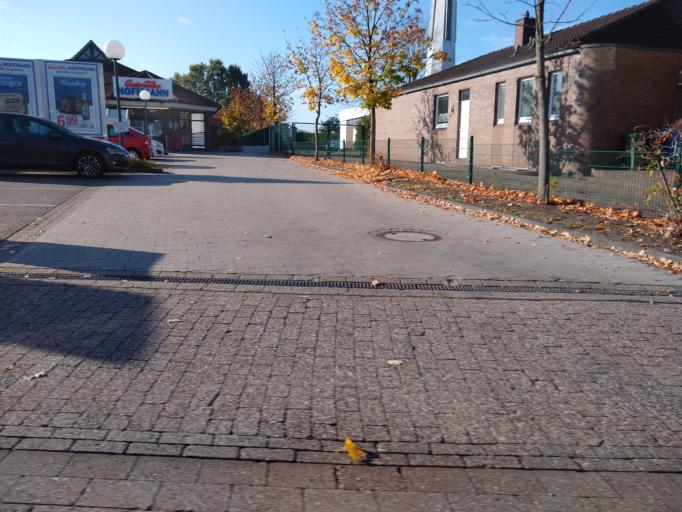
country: DE
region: Lower Saxony
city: Oldenburg
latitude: 53.1850
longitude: 8.2029
